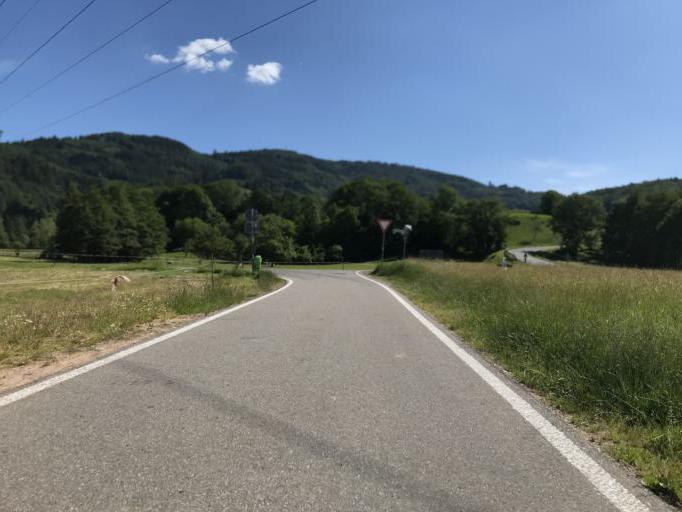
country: DE
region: Baden-Wuerttemberg
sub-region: Freiburg Region
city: Hausen
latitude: 47.6763
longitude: 7.8466
